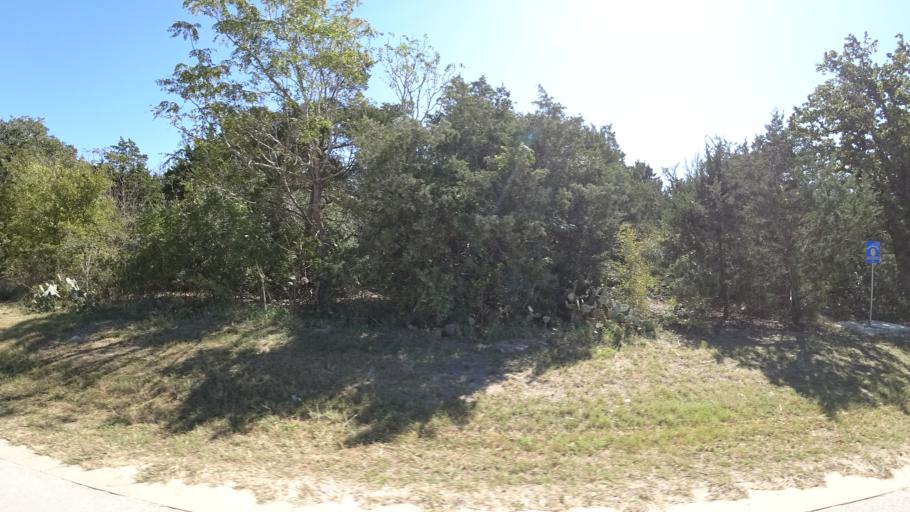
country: US
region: Texas
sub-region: Travis County
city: Hornsby Bend
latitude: 30.2738
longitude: -97.6077
